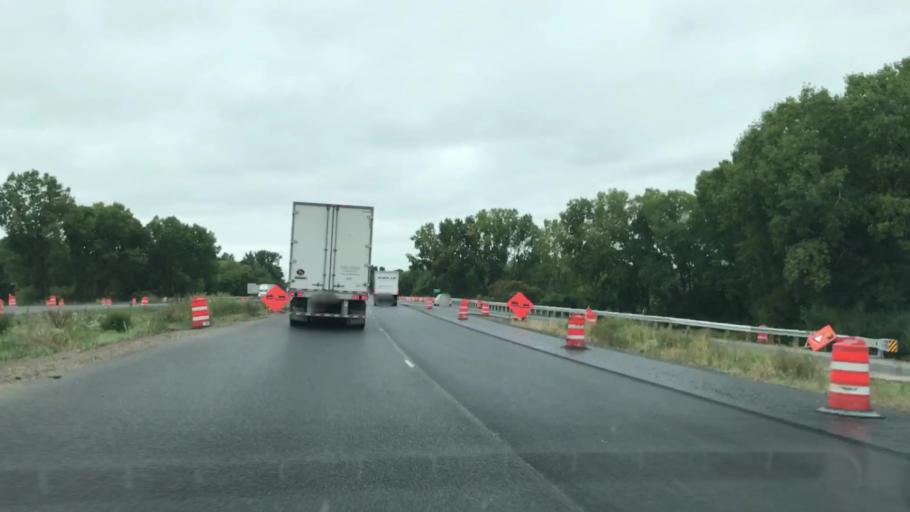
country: US
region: Wisconsin
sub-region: Brown County
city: Suamico
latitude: 44.6333
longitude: -88.0469
